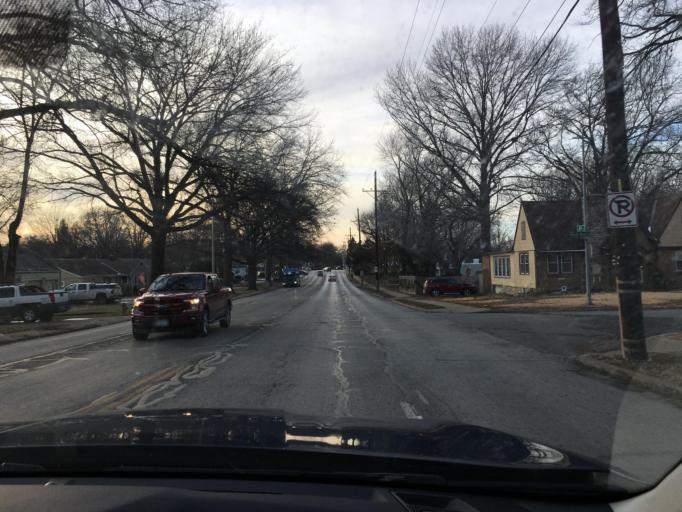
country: US
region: Kansas
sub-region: Johnson County
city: Leawood
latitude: 38.9746
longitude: -94.6041
